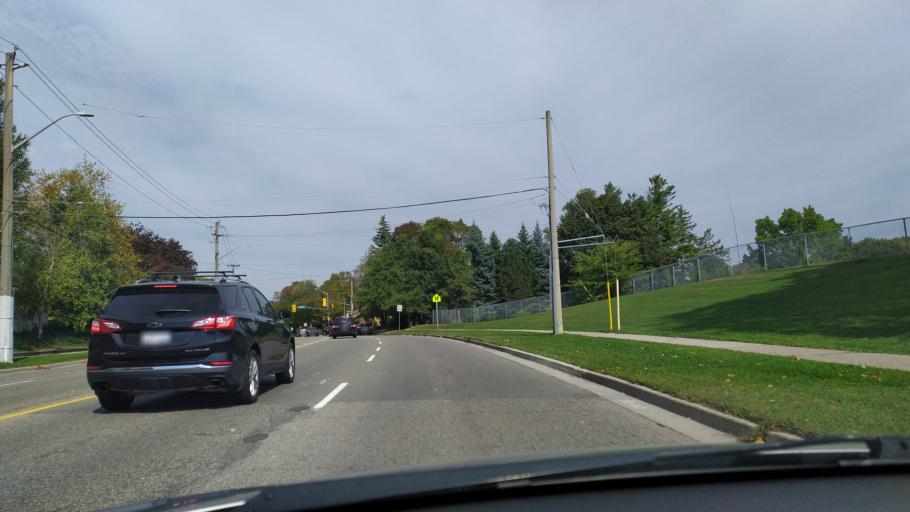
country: CA
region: Ontario
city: Waterloo
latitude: 43.4484
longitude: -80.5232
